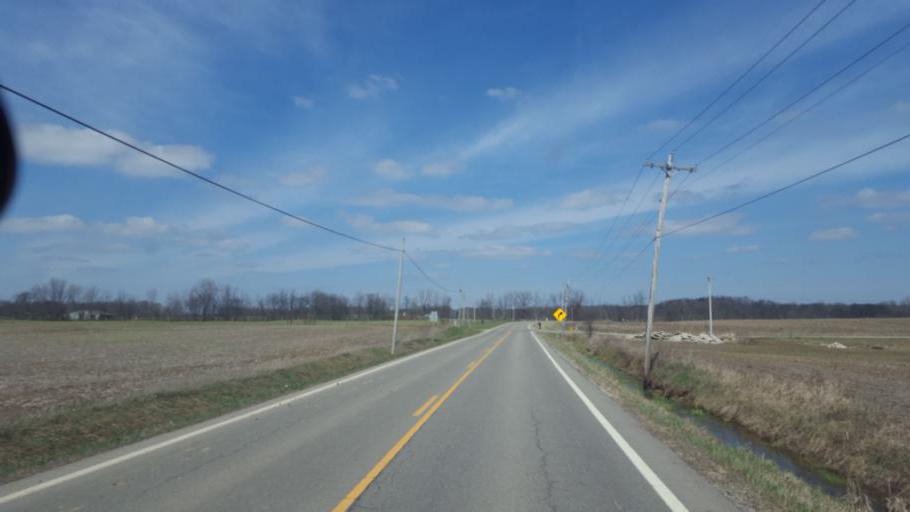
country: US
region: Ohio
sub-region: Richland County
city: Lincoln Heights
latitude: 40.8355
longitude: -82.4772
